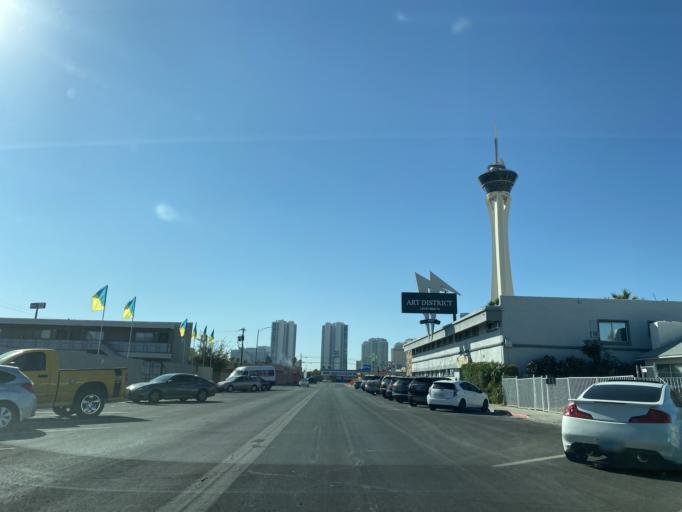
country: US
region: Nevada
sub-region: Clark County
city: Las Vegas
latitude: 36.1531
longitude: -115.1527
